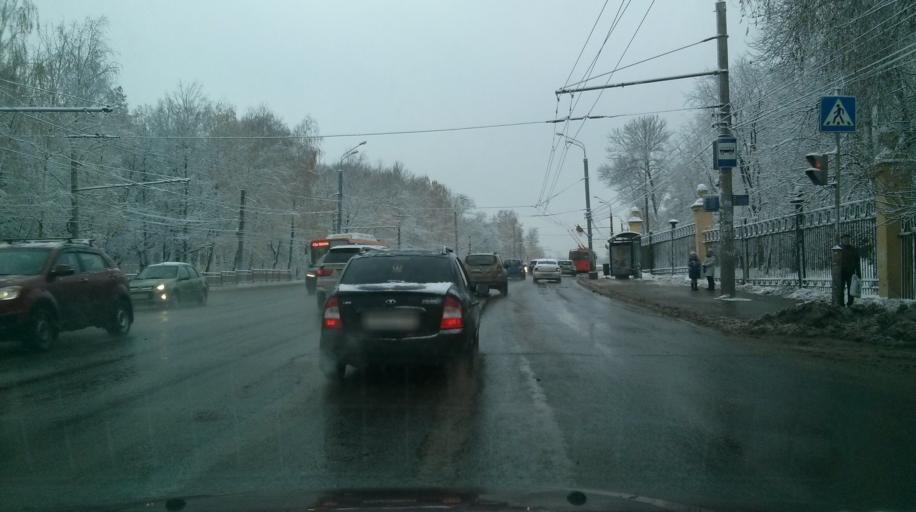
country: RU
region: Nizjnij Novgorod
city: Nizhniy Novgorod
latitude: 56.2616
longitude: 43.9735
